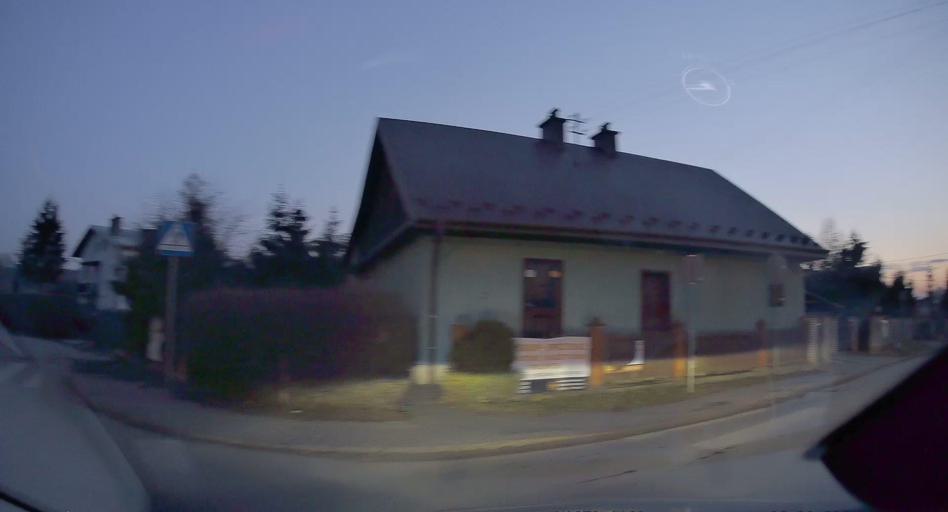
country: PL
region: Subcarpathian Voivodeship
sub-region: Powiat debicki
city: Debica
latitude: 50.0301
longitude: 21.3946
